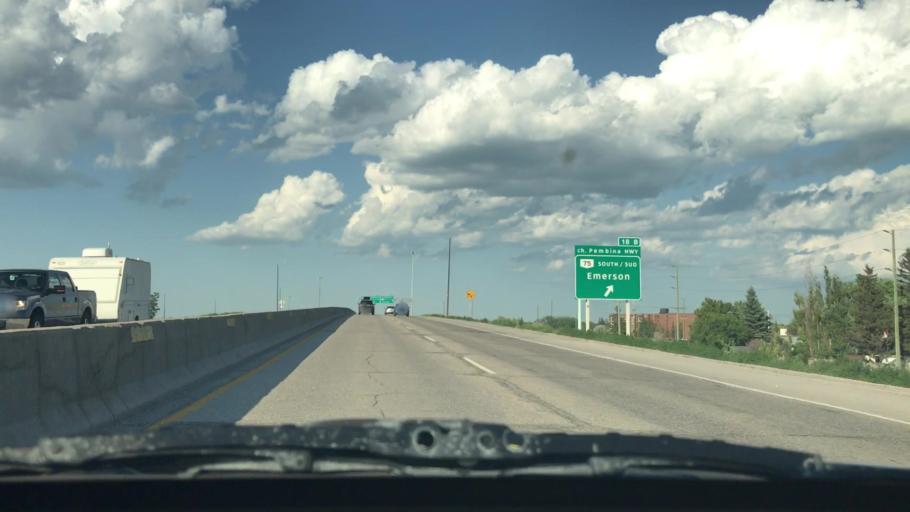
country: CA
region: Manitoba
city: Winnipeg
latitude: 49.7743
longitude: -97.1642
